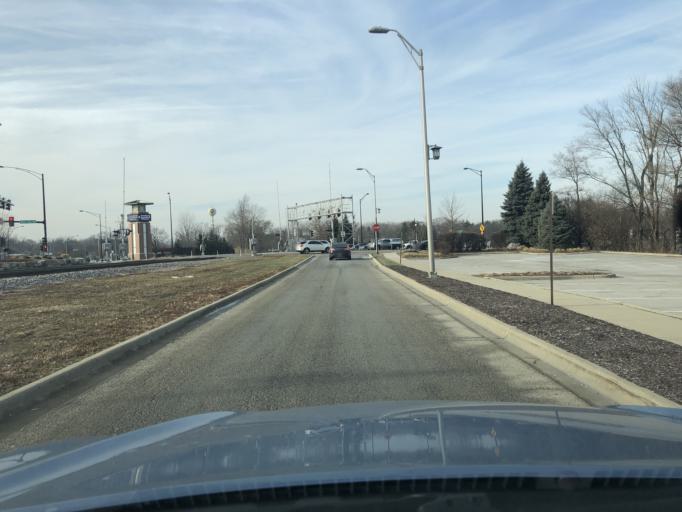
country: US
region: Illinois
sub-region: DuPage County
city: Wood Dale
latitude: 41.9635
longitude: -87.9779
